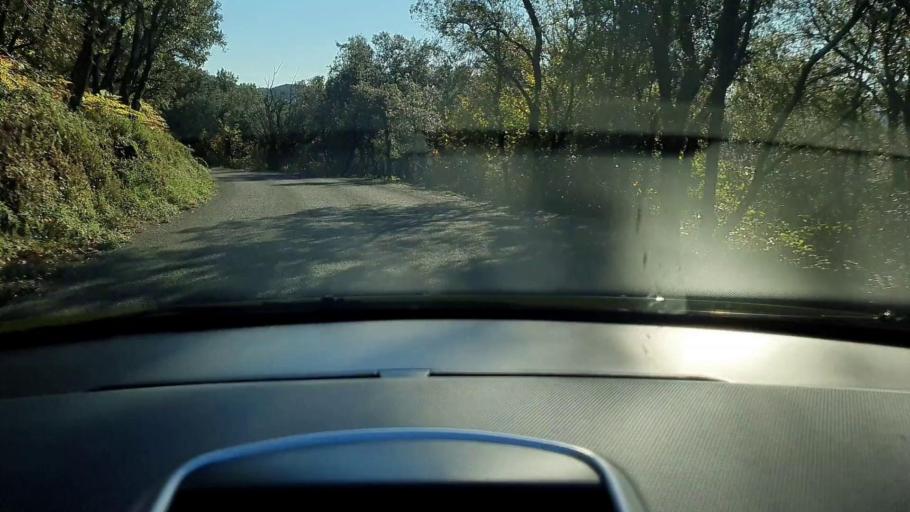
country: FR
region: Languedoc-Roussillon
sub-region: Departement du Gard
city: Sumene
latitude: 44.0300
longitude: 3.6938
